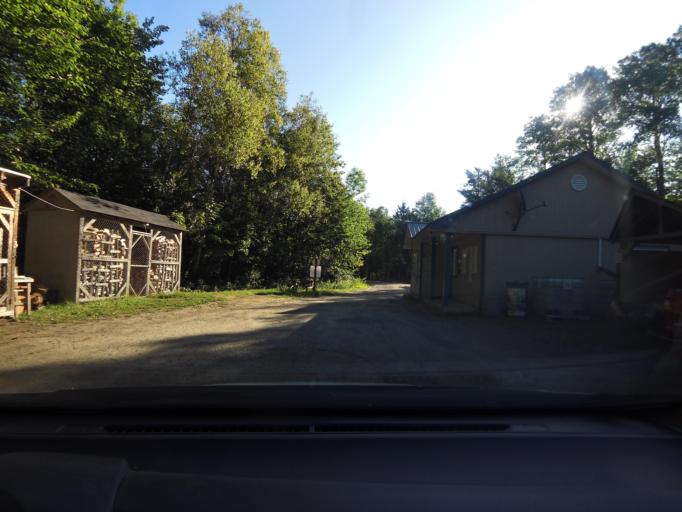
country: CA
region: Quebec
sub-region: Mauricie
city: Becancour
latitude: 46.5452
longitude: -72.3974
